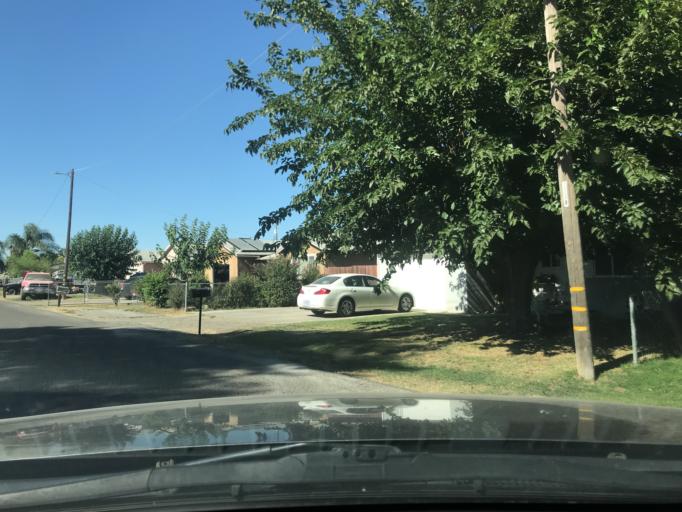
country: US
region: California
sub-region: Merced County
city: Merced
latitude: 37.3177
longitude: -120.5239
